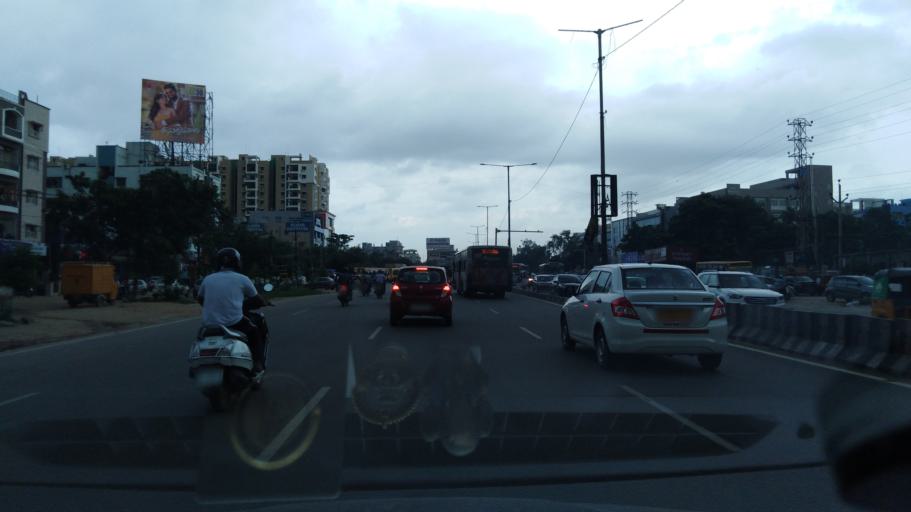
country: IN
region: Telangana
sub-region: Medak
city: Serilingampalle
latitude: 17.4951
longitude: 78.3440
